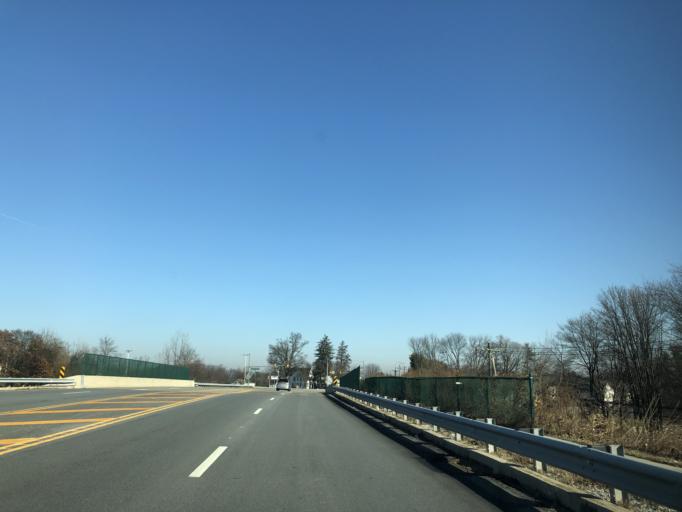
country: US
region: Pennsylvania
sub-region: Chester County
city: Chester Springs
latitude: 40.0640
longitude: -75.6505
